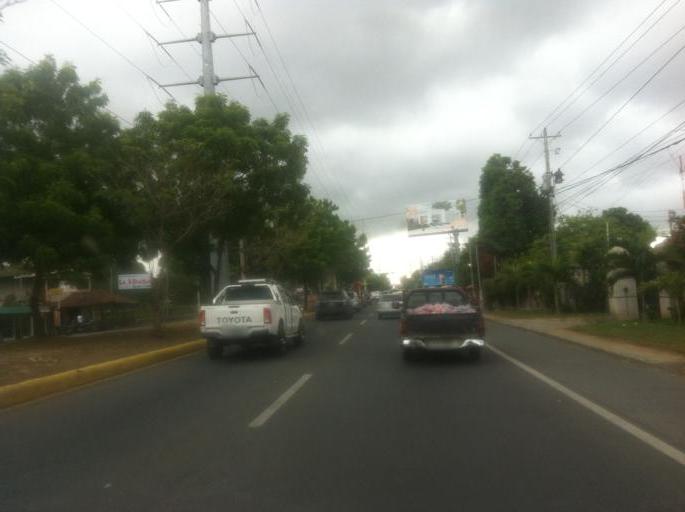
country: NI
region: Masaya
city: Ticuantepe
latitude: 12.0734
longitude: -86.2188
